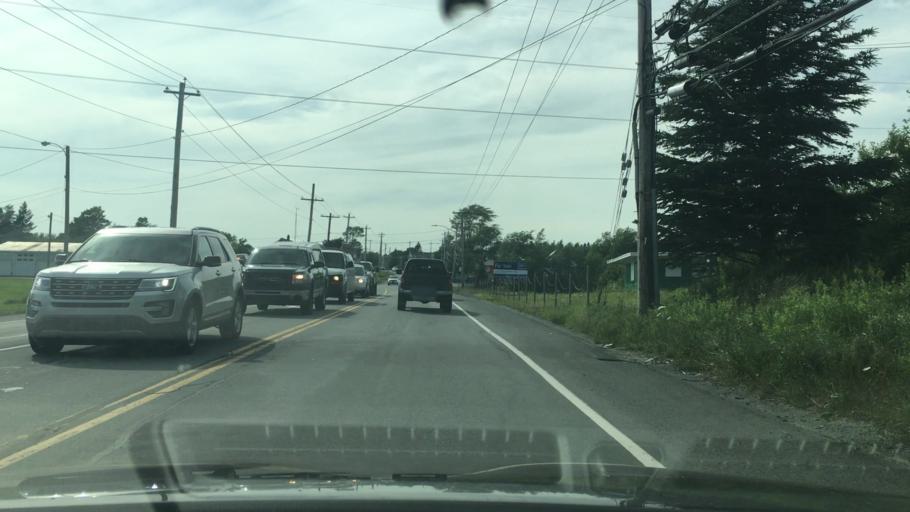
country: CA
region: Nova Scotia
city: Dartmouth
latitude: 44.7325
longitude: -63.7598
